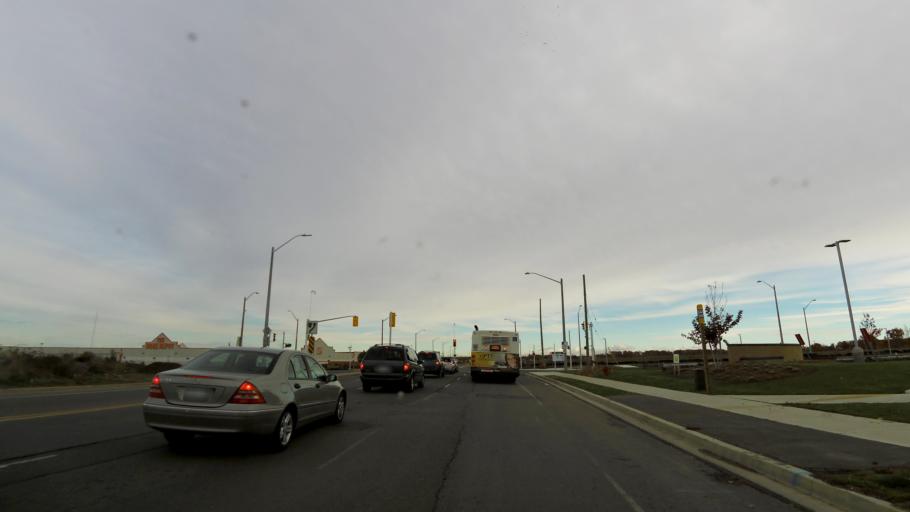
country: CA
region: Ontario
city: Hamilton
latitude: 43.1928
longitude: -79.8162
